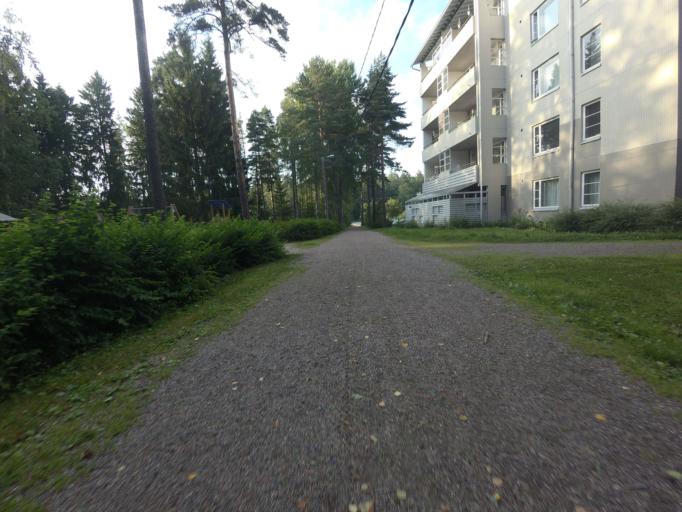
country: FI
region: Uusimaa
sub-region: Helsinki
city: Kauniainen
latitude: 60.1738
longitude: 24.7082
